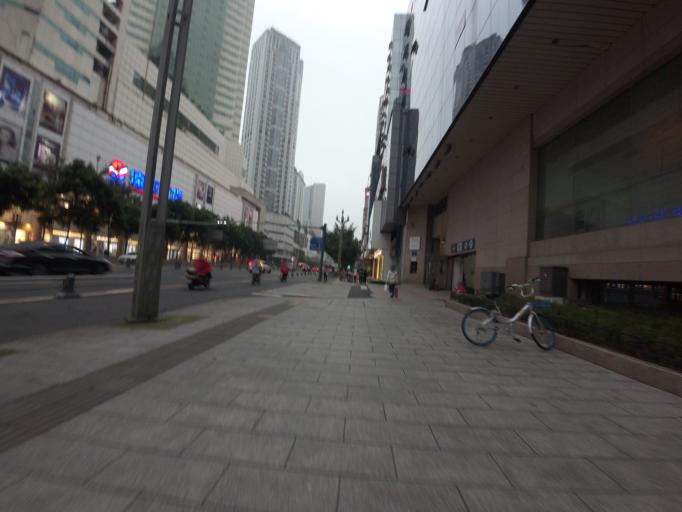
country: CN
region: Sichuan
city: Chengdu
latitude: 30.6720
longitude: 104.0636
